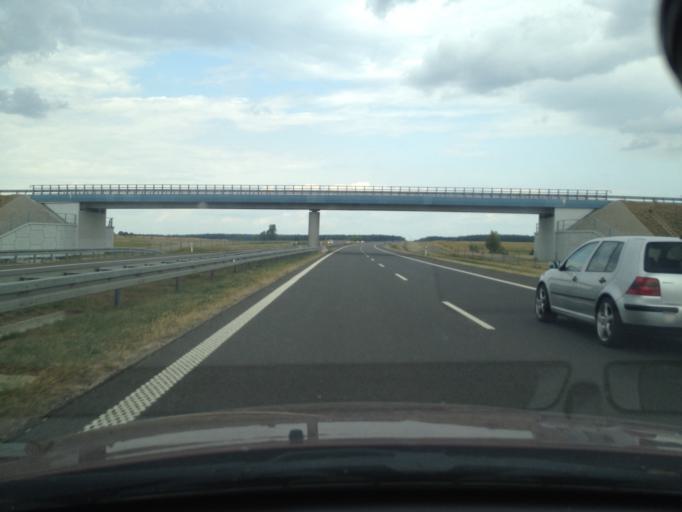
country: PL
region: West Pomeranian Voivodeship
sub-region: Powiat pyrzycki
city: Bielice
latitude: 53.1363
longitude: 14.7230
